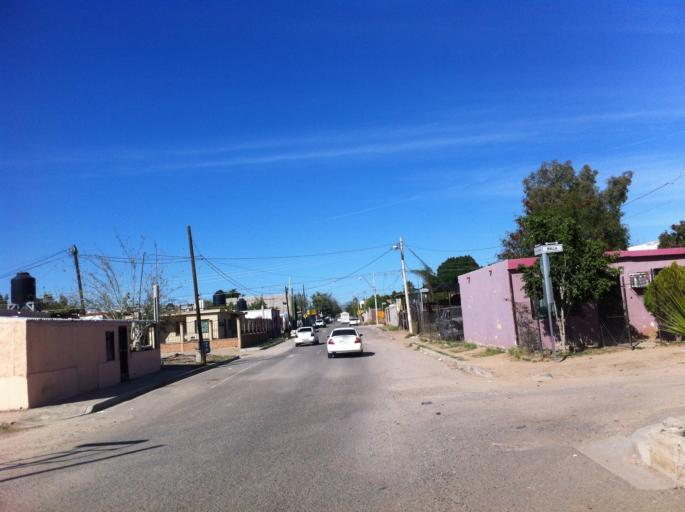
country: MX
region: Sonora
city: Hermosillo
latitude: 29.1014
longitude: -111.0114
